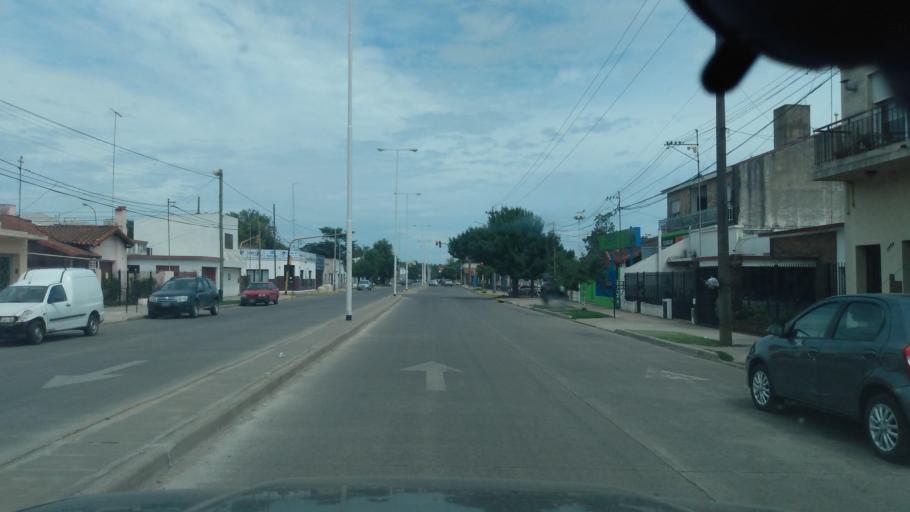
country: AR
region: Buenos Aires
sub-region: Partido de Lujan
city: Lujan
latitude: -34.5630
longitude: -59.1029
